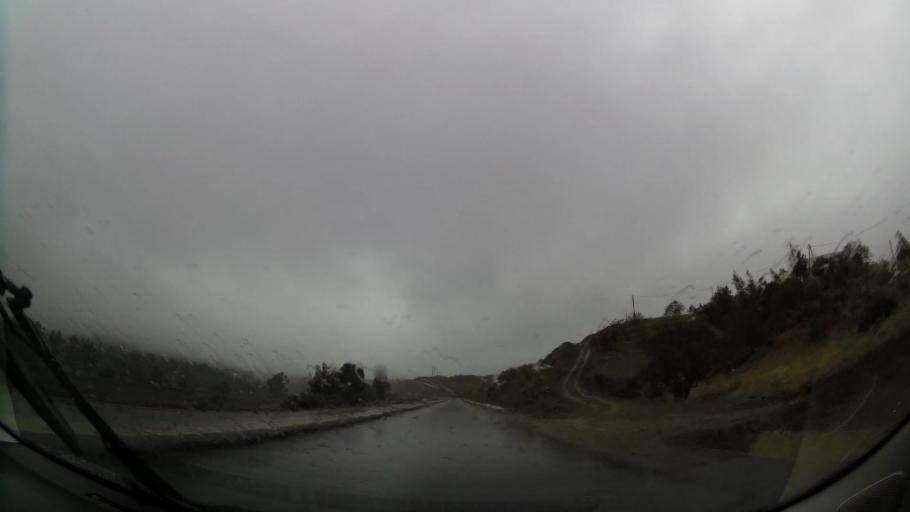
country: MA
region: Taza-Al Hoceima-Taounate
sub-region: Taza
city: Aknoul
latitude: 34.7985
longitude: -3.7429
